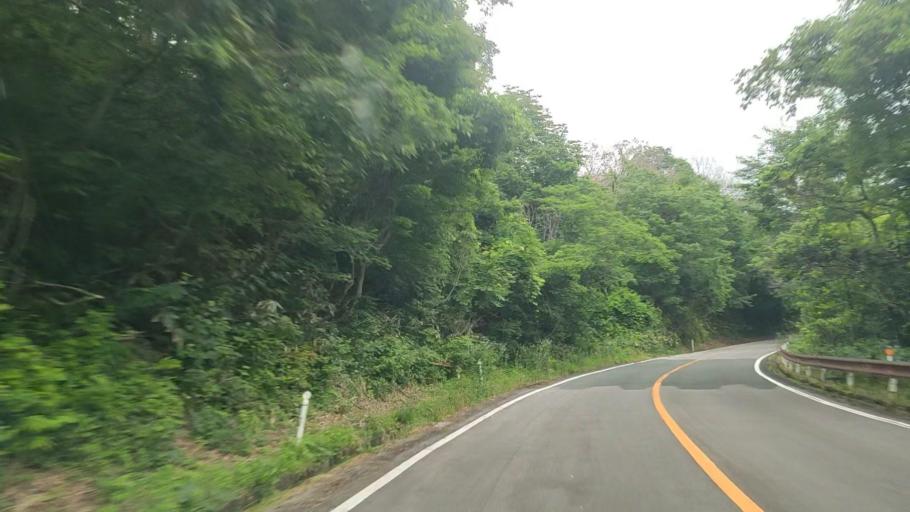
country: JP
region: Tottori
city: Kurayoshi
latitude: 35.3046
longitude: 133.6192
